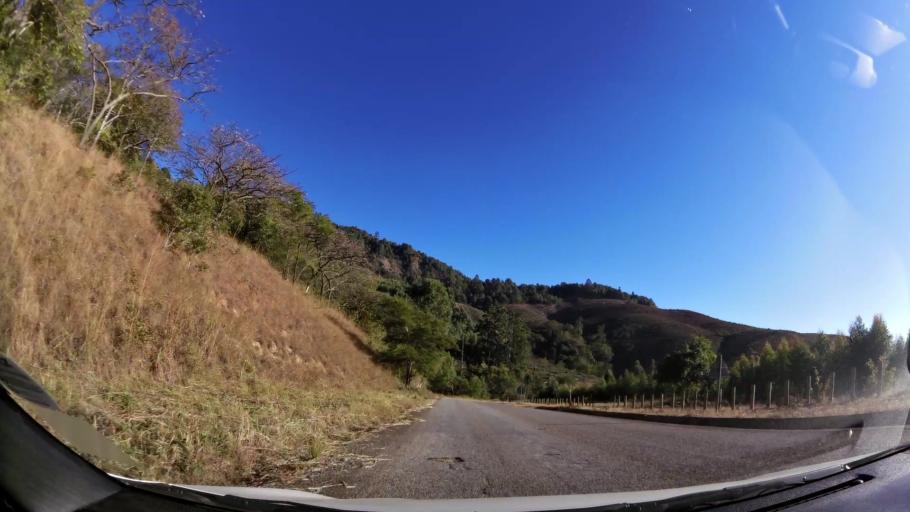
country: ZA
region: Limpopo
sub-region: Mopani District Municipality
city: Tzaneen
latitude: -23.9490
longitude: 30.0140
